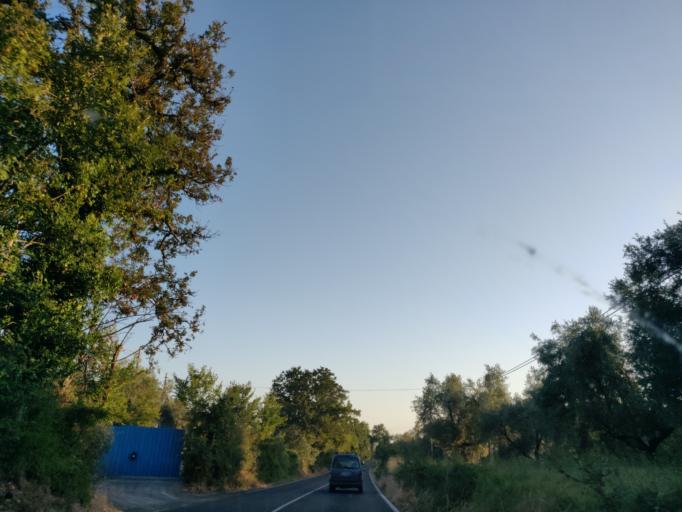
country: IT
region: Latium
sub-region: Provincia di Viterbo
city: Canino
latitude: 42.4374
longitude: 11.7274
